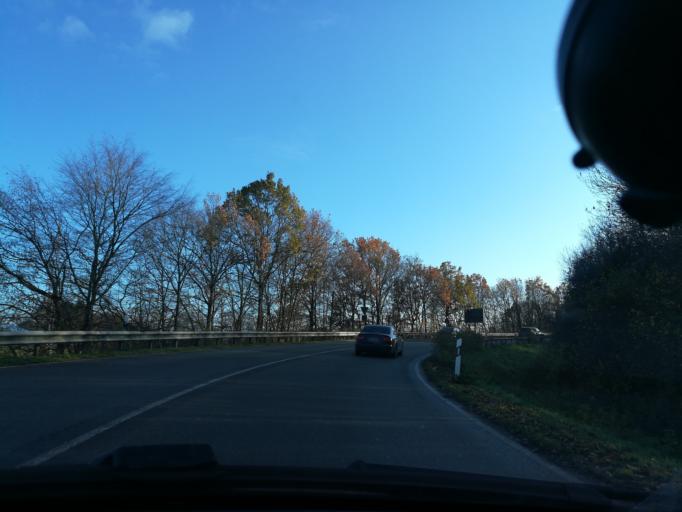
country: DE
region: North Rhine-Westphalia
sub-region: Regierungsbezirk Detmold
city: Petershagen
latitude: 52.3776
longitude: 8.9985
